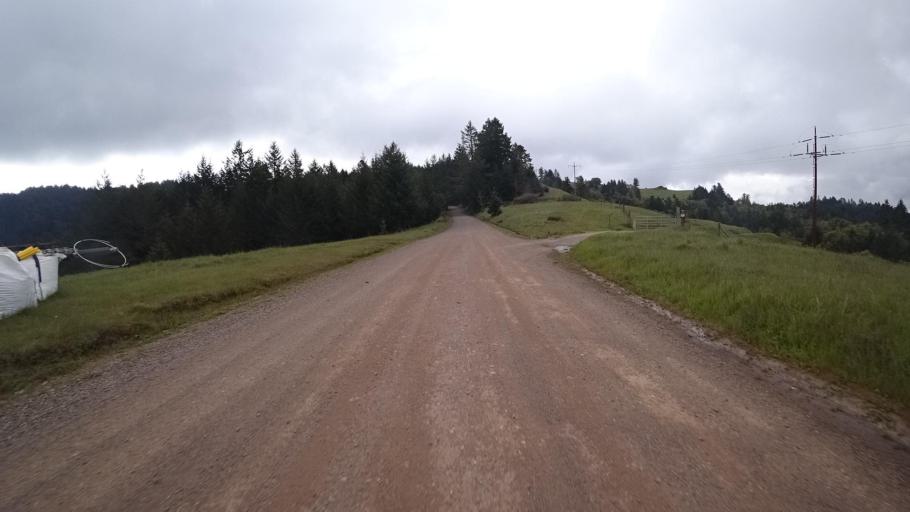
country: US
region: California
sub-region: Humboldt County
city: Redway
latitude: 40.2173
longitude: -123.7529
